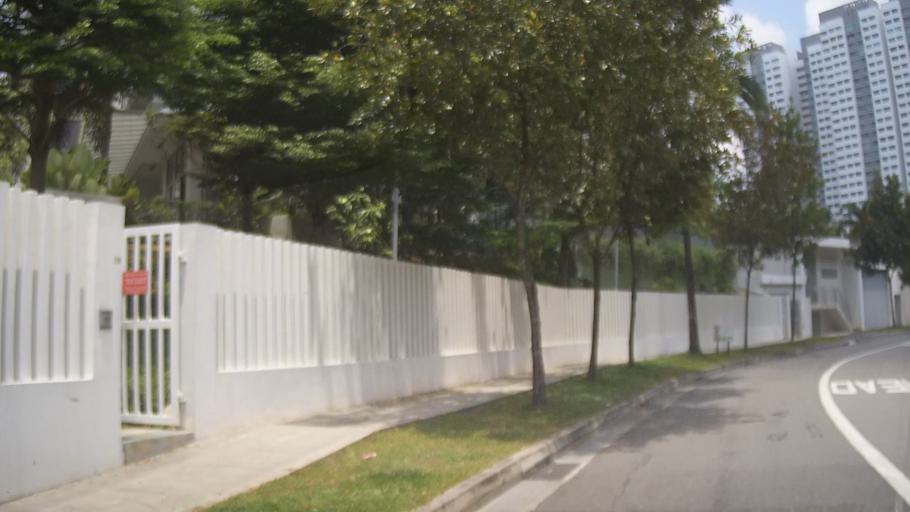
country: SG
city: Singapore
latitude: 1.3266
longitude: 103.8629
